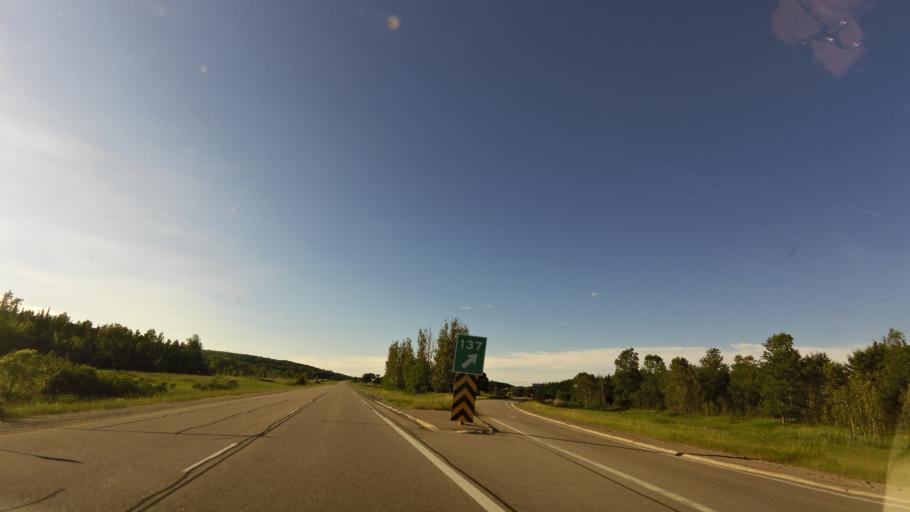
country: CA
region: Ontario
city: Orillia
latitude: 44.6720
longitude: -79.6437
